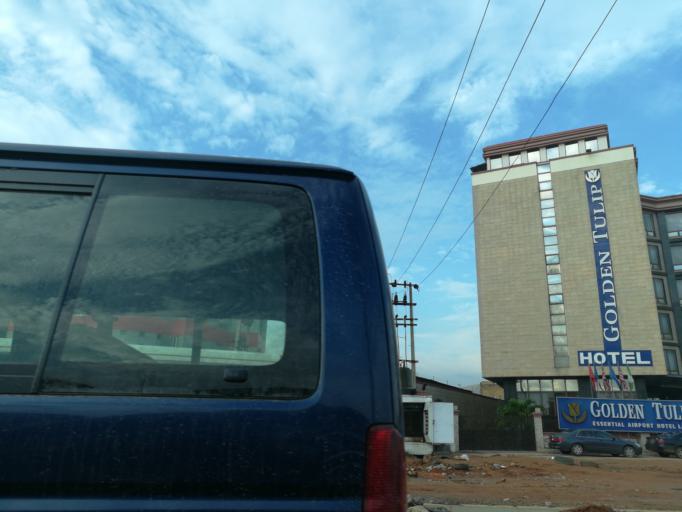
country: NG
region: Lagos
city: Oshodi
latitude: 6.5520
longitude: 3.3295
